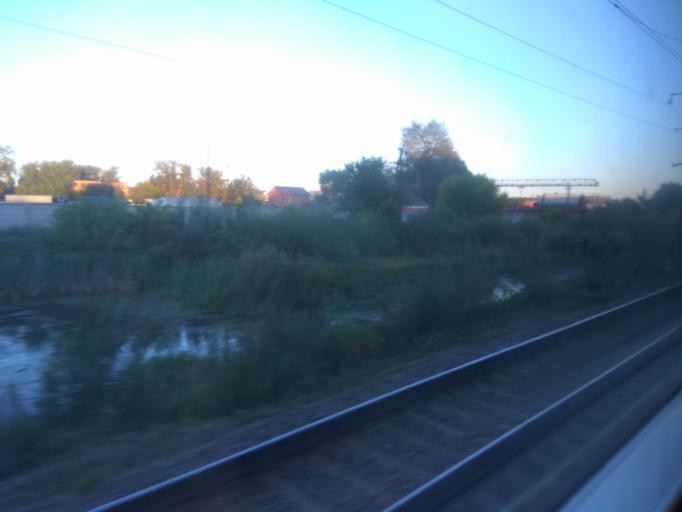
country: RU
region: Moskovskaya
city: Elektrostal'
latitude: 55.7751
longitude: 38.4660
